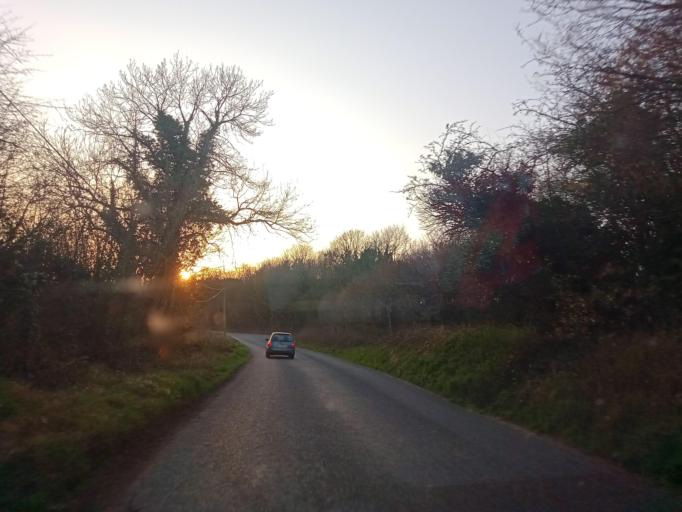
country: IE
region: Leinster
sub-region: Kilkenny
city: Castlecomer
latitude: 52.8633
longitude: -7.2715
